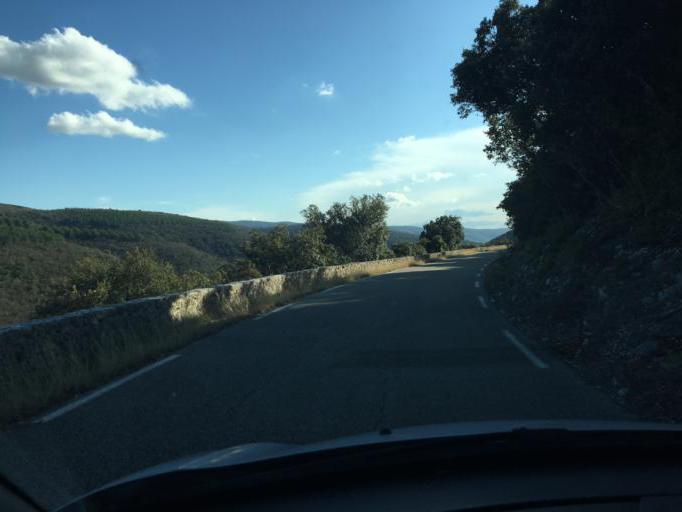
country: FR
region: Provence-Alpes-Cote d'Azur
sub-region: Departement du Vaucluse
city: Villes-sur-Auzon
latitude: 44.0454
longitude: 5.2759
